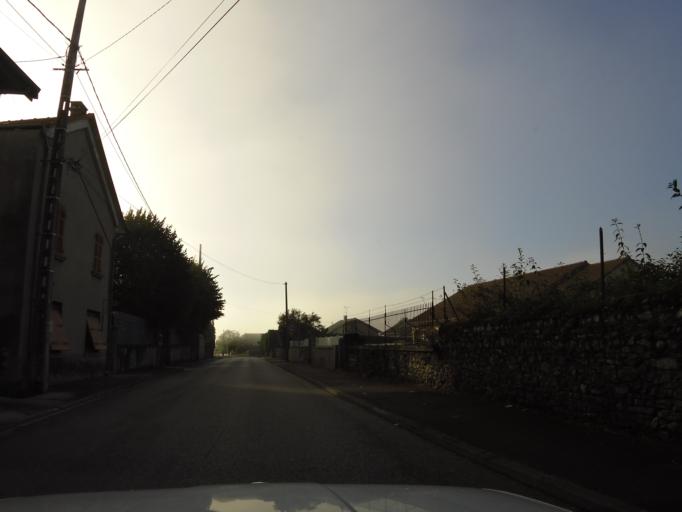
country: FR
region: Rhone-Alpes
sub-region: Departement de l'Isere
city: Bouvesse-Quirieu
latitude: 45.8053
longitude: 5.4539
